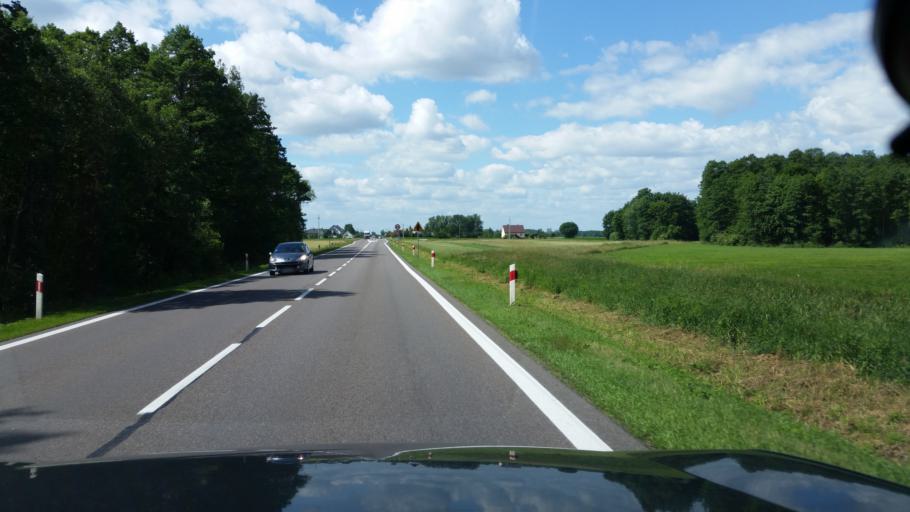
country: PL
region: Podlasie
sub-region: Powiat grajewski
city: Rajgrod
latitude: 53.6876
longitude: 22.6271
